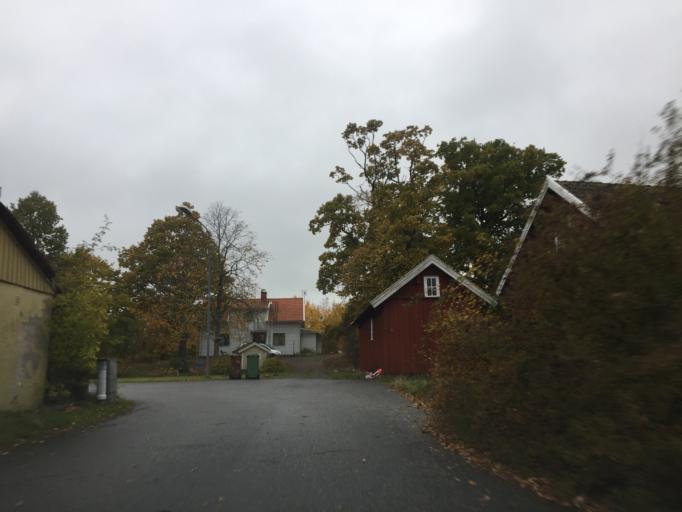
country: SE
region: Vaestra Goetaland
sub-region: Trollhattan
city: Sjuntorp
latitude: 58.1607
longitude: 12.3095
